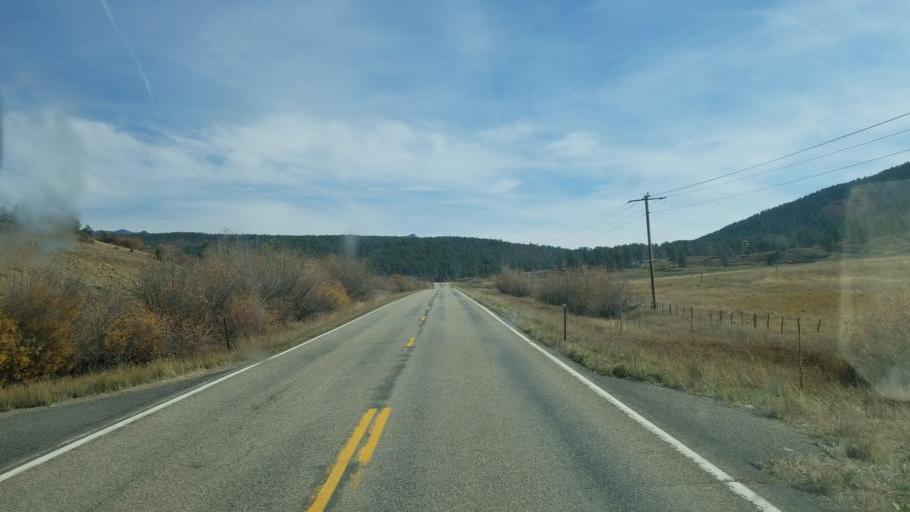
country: US
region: New Mexico
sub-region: Rio Arriba County
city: Dulce
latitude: 37.0804
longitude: -106.8761
